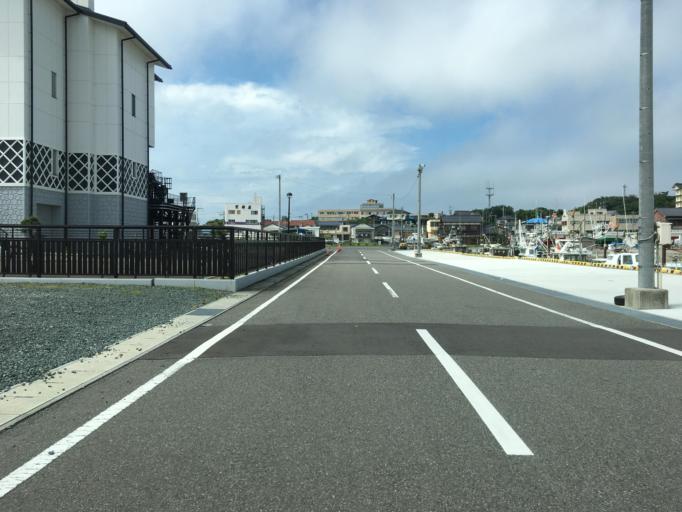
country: JP
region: Miyagi
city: Marumori
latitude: 37.8210
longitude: 140.9693
